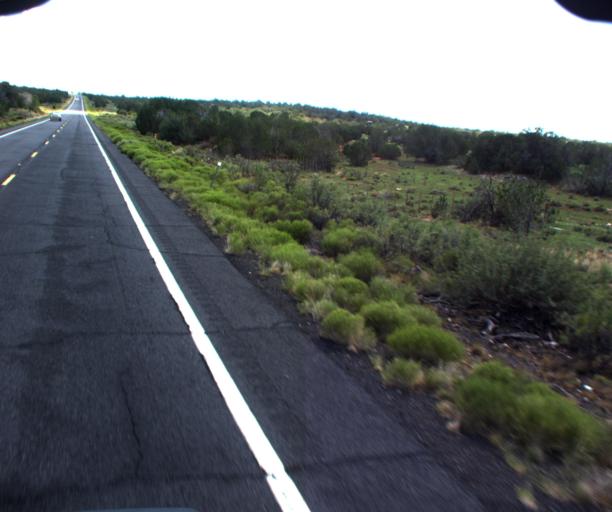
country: US
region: Arizona
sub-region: Coconino County
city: Williams
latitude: 35.5182
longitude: -112.1703
